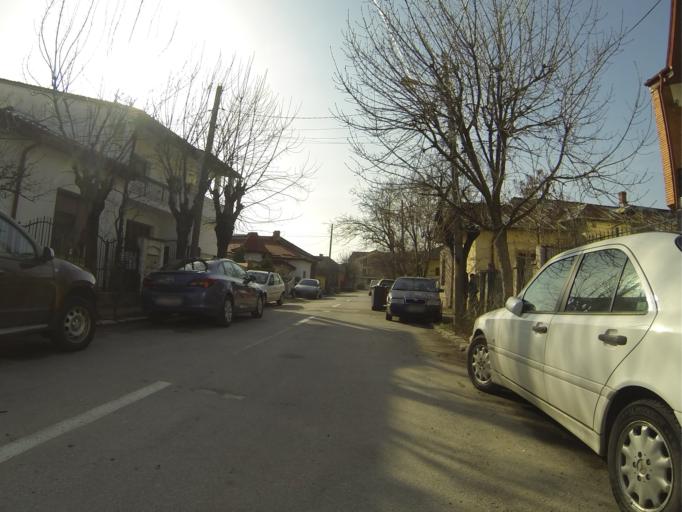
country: RO
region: Dolj
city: Craiova
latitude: 44.3139
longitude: 23.8142
